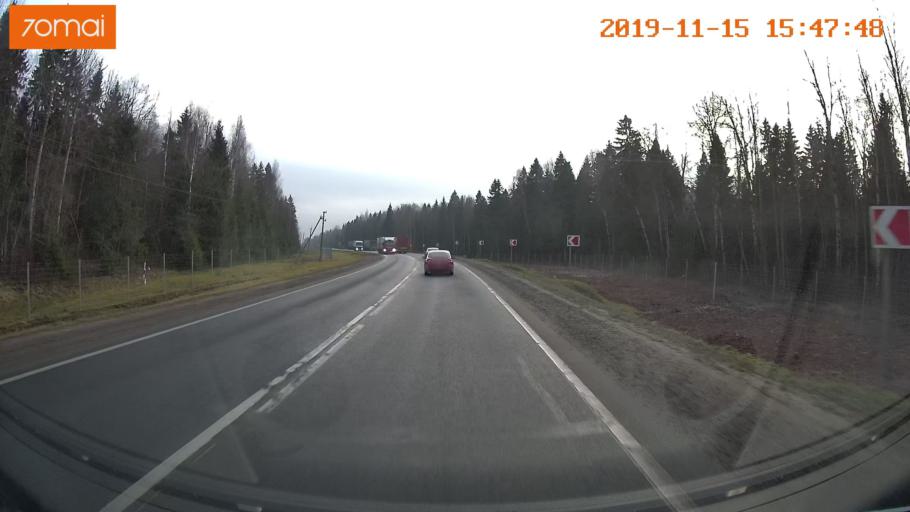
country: RU
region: Jaroslavl
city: Danilov
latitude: 57.9344
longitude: 40.0069
